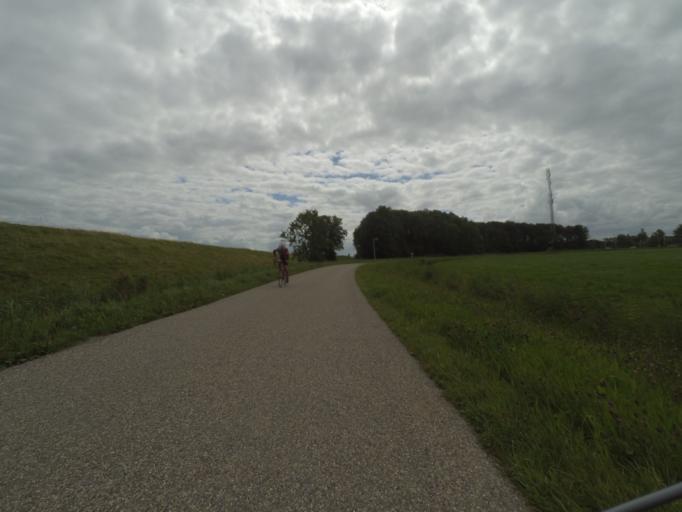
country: NL
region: Friesland
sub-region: Gemeente Kollumerland en Nieuwkruisland
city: Kollum
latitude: 53.3268
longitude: 6.1549
